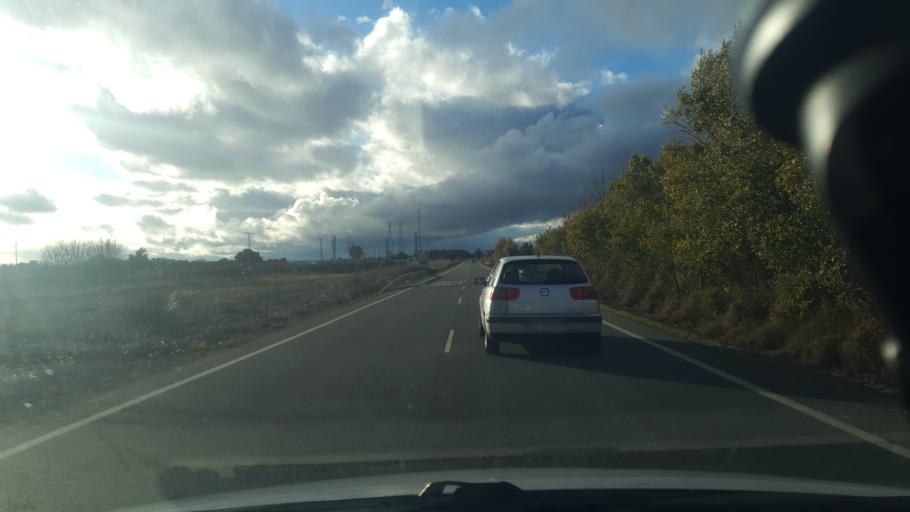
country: ES
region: Castille and Leon
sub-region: Provincia de Segovia
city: Nava de la Asuncion
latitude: 41.1559
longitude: -4.4954
